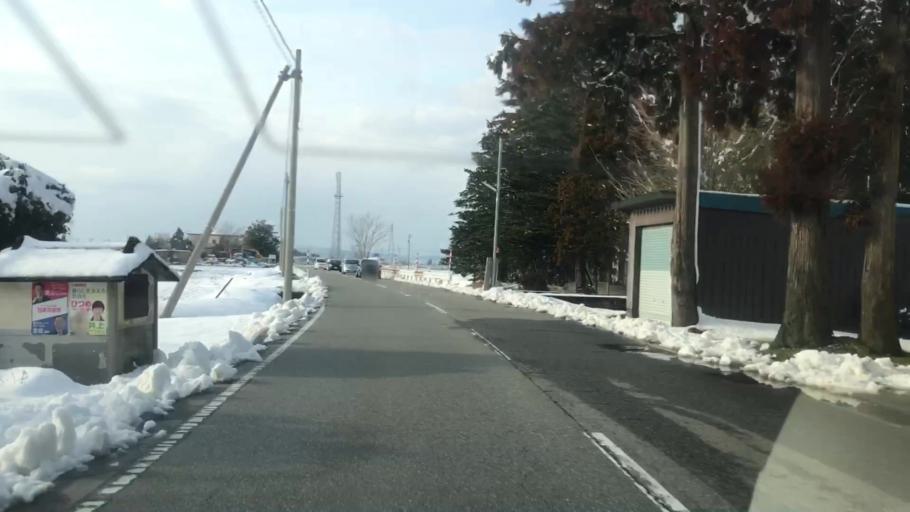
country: JP
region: Toyama
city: Toyama-shi
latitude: 36.6382
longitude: 137.2622
